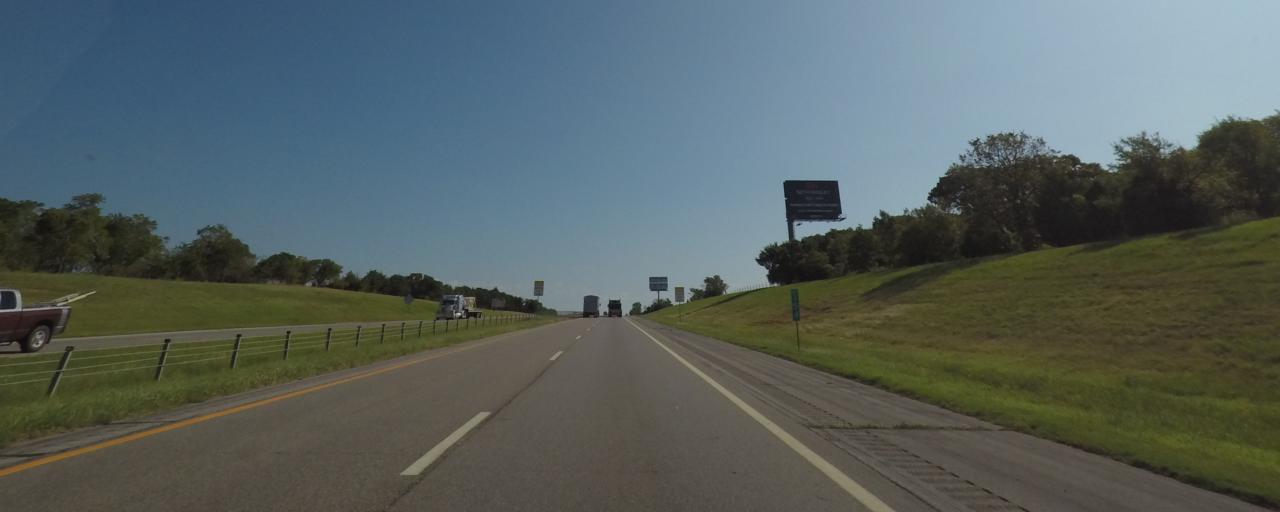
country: US
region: Oklahoma
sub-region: Logan County
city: Guthrie
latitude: 35.8282
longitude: -97.4051
